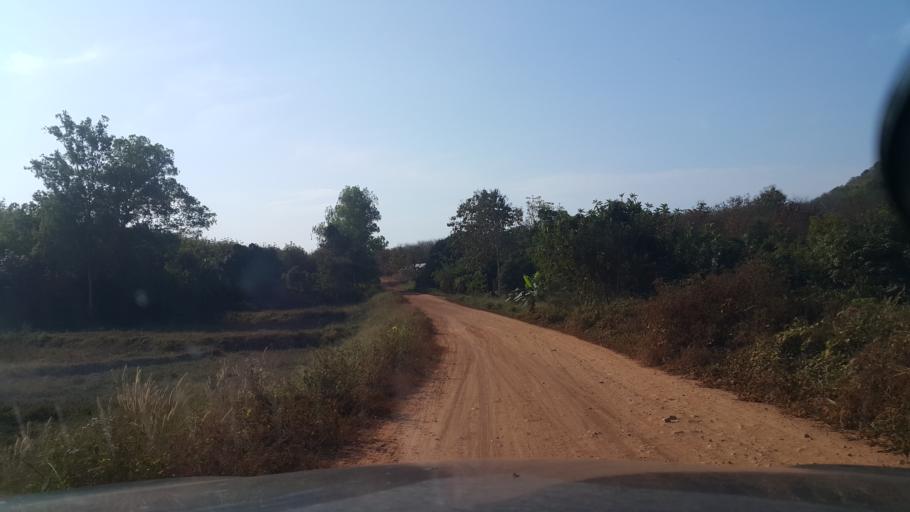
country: TH
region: Loei
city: Chiang Khan
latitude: 17.8144
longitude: 101.6169
